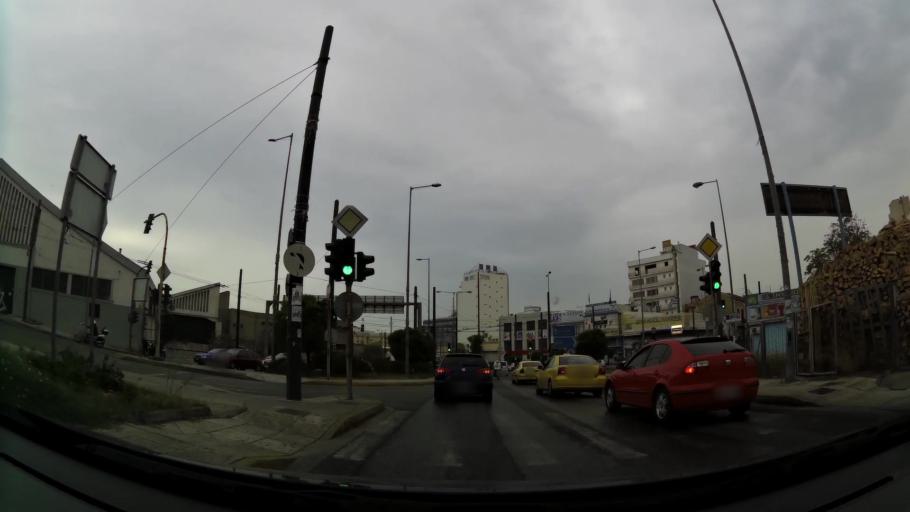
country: GR
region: Attica
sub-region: Nomos Attikis
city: Piraeus
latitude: 37.9483
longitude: 23.6474
